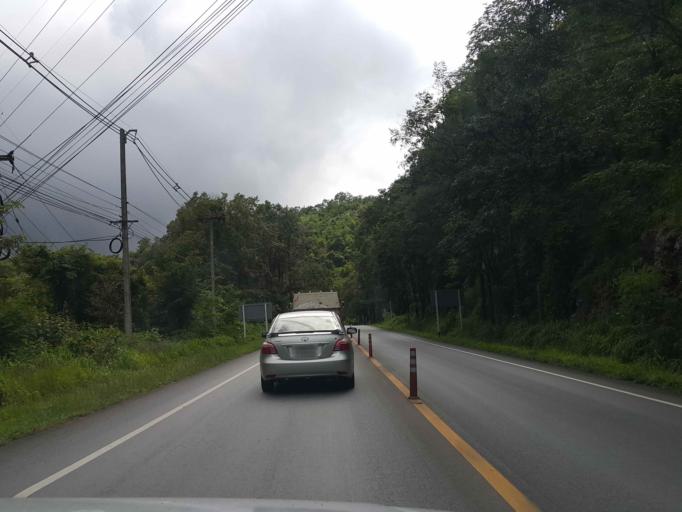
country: TH
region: Tak
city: Tak
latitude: 16.8010
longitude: 98.9554
